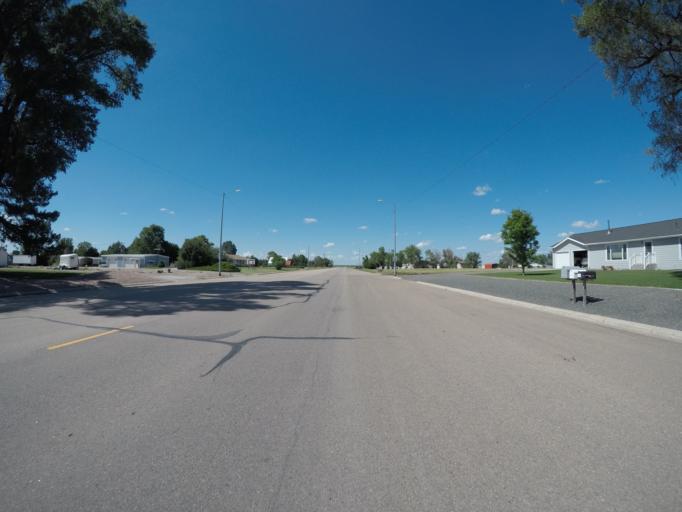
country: US
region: Nebraska
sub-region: Chase County
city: Imperial
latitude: 40.5285
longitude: -101.6432
